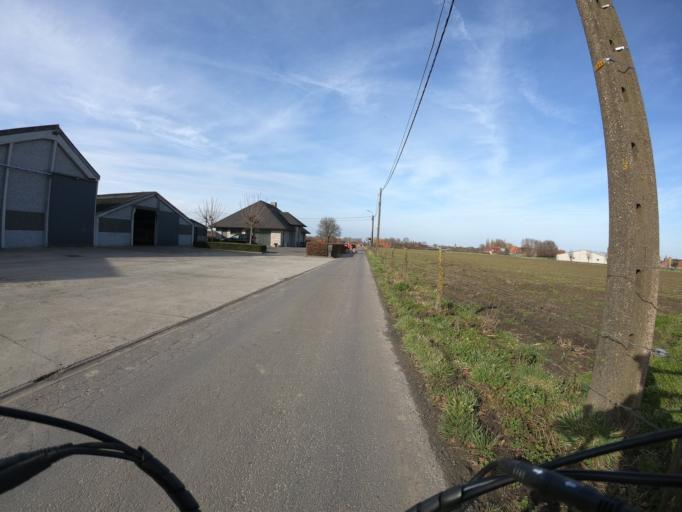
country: BE
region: Flanders
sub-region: Provincie West-Vlaanderen
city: Ledegem
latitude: 50.8945
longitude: 3.1069
